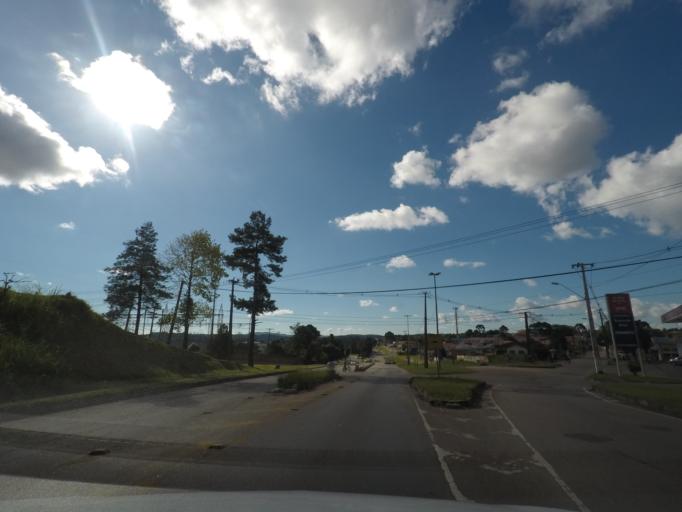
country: BR
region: Parana
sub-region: Curitiba
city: Curitiba
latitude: -25.3723
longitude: -49.2745
